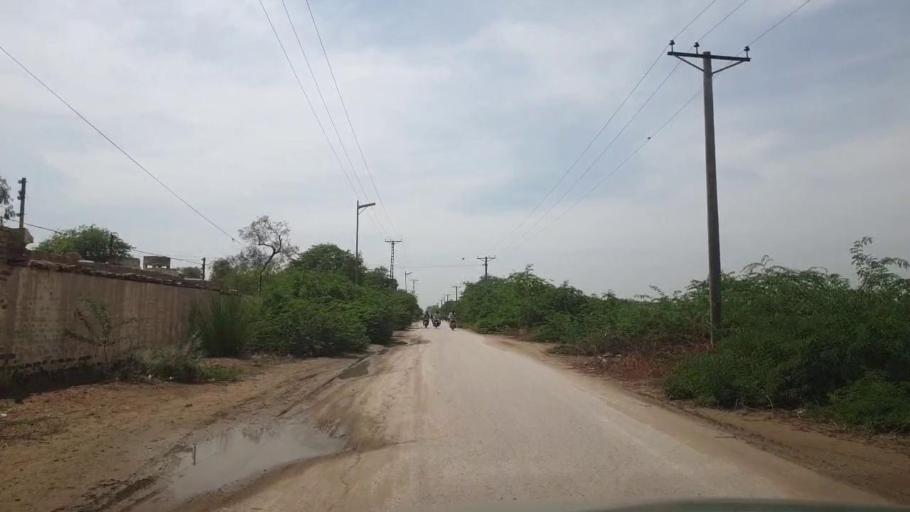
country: PK
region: Sindh
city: Kot Diji
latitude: 27.1622
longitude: 68.9558
